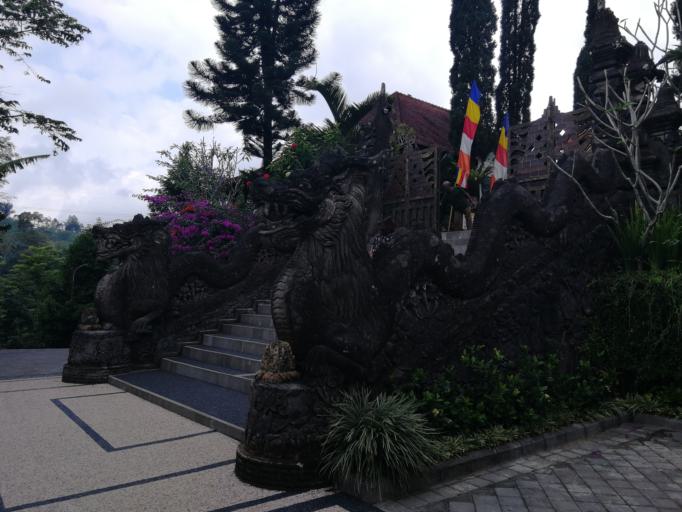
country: ID
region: Bali
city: Bantiran
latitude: -8.3193
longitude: 115.0179
